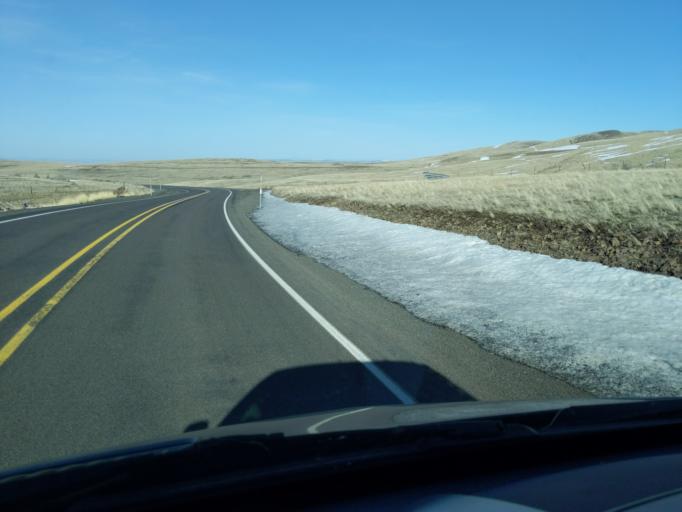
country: US
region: Oregon
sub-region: Umatilla County
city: Pilot Rock
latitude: 45.3043
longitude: -119.0045
